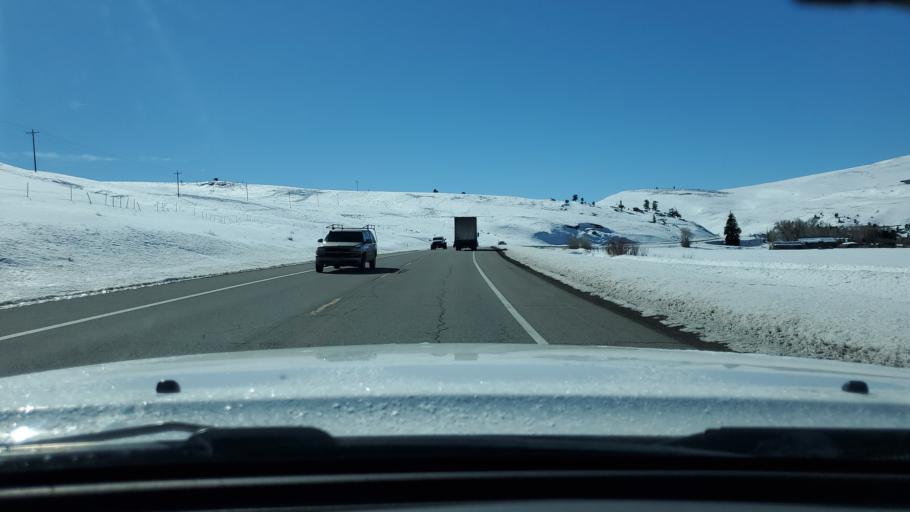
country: US
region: Colorado
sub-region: Gunnison County
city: Gunnison
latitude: 38.6975
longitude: -106.8494
